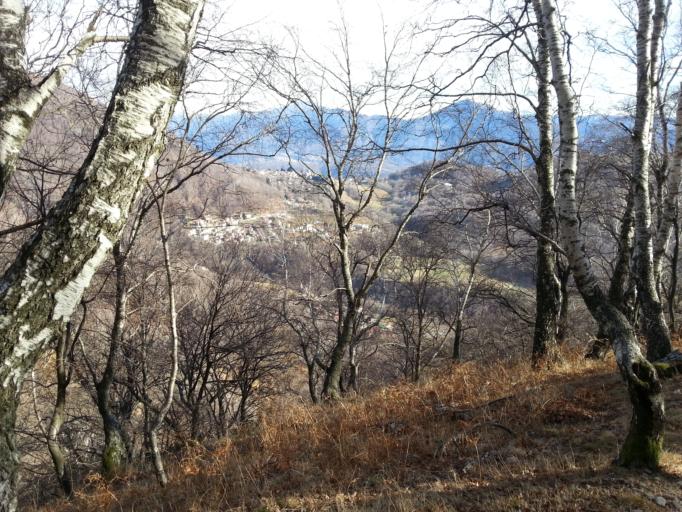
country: CH
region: Ticino
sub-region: Lugano District
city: Gravesano
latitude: 46.0460
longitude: 8.8742
